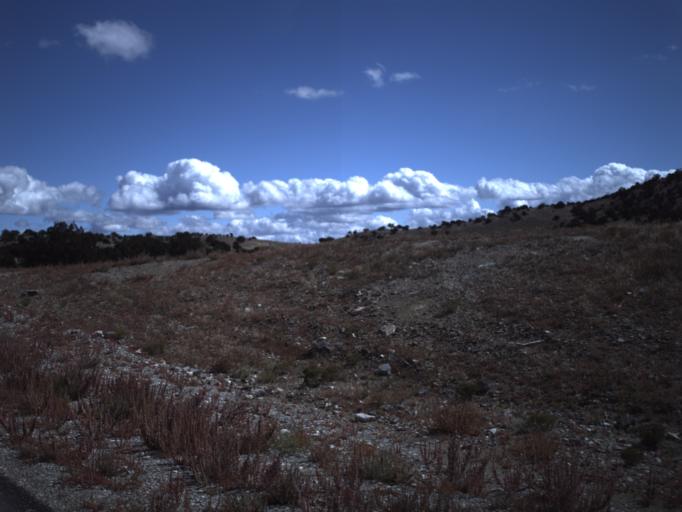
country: US
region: Utah
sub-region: Beaver County
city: Milford
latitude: 38.5172
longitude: -113.5508
